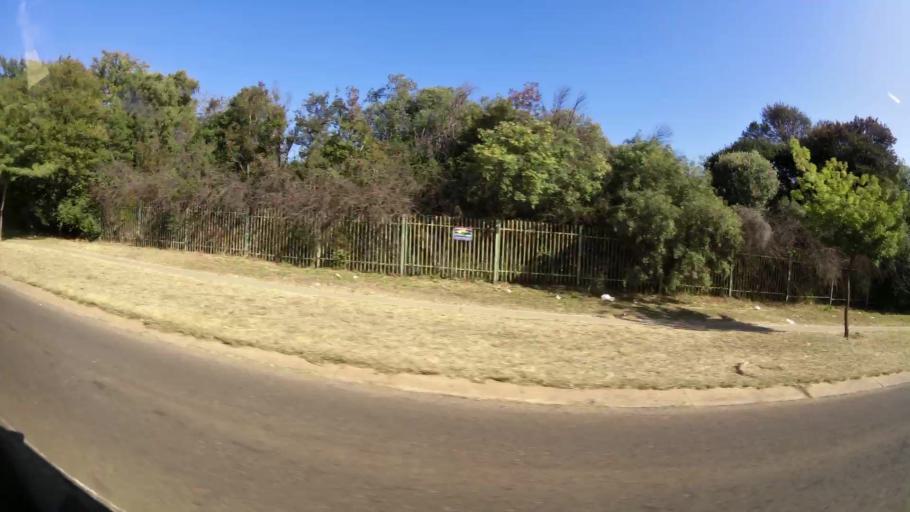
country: ZA
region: Gauteng
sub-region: City of Tshwane Metropolitan Municipality
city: Pretoria
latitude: -25.6625
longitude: 28.2439
